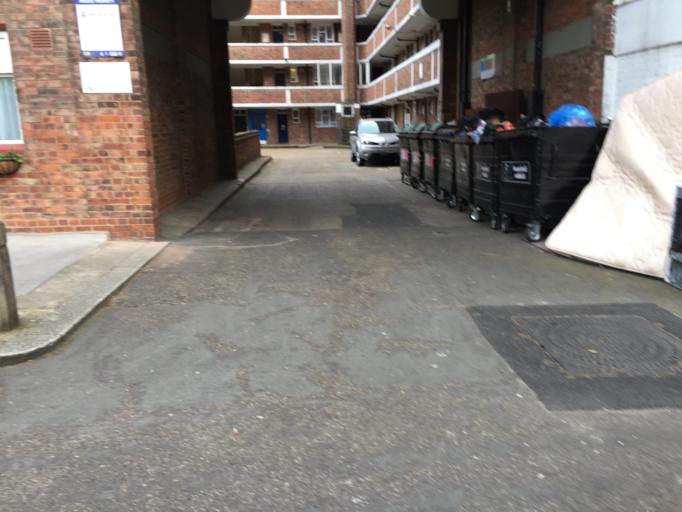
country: GB
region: England
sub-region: Greater London
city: City of Westminster
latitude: 51.4869
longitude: -0.1323
